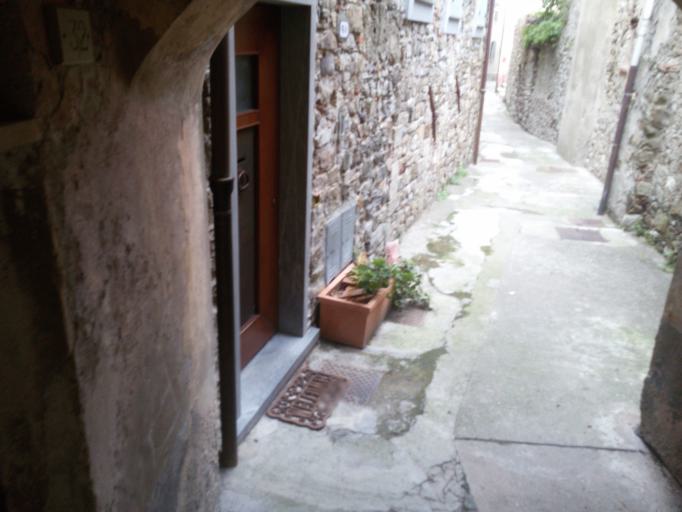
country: IT
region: Liguria
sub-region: Provincia di La Spezia
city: Santo Stefano di Magra
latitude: 44.1561
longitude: 9.9449
